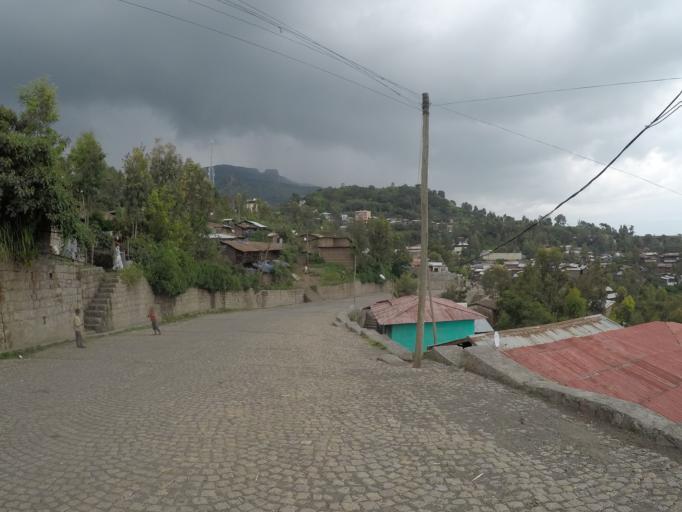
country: ET
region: Amhara
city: Lalibela
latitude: 12.0378
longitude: 39.0435
